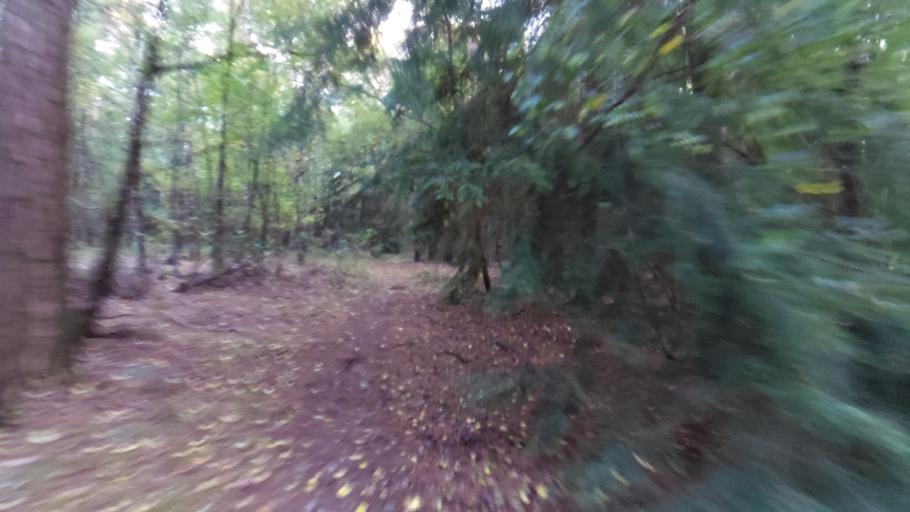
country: NL
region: Gelderland
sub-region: Gemeente Ede
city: Wekerom
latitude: 52.0847
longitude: 5.6903
